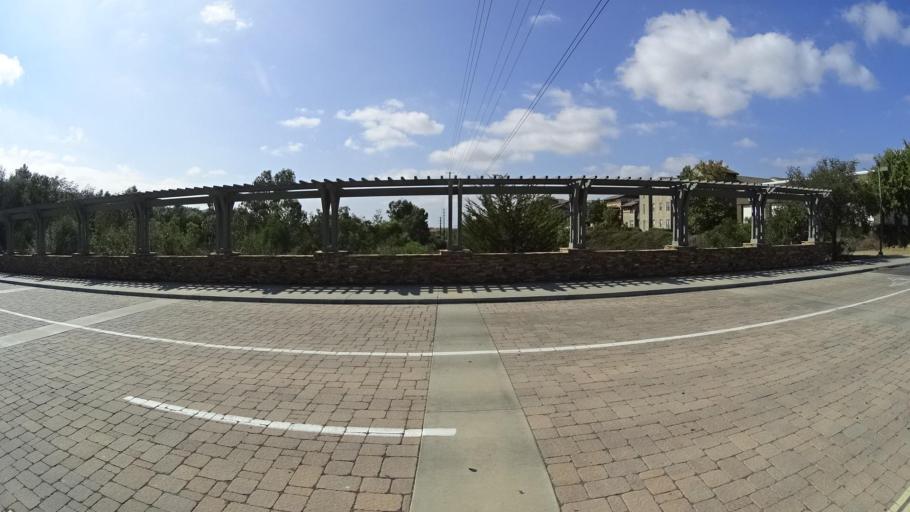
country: US
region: California
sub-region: San Diego County
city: Fairbanks Ranch
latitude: 33.0187
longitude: -117.1151
